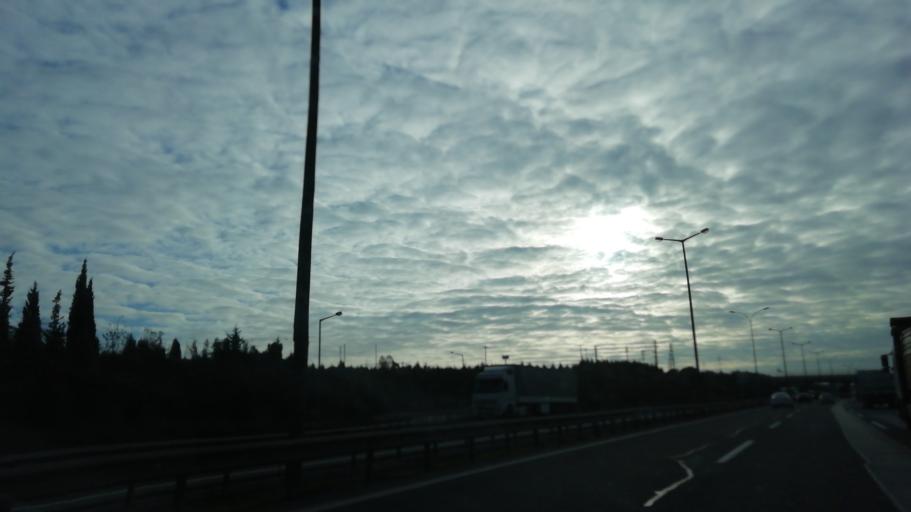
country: TR
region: Kocaeli
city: Balcik
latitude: 40.8701
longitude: 29.3961
